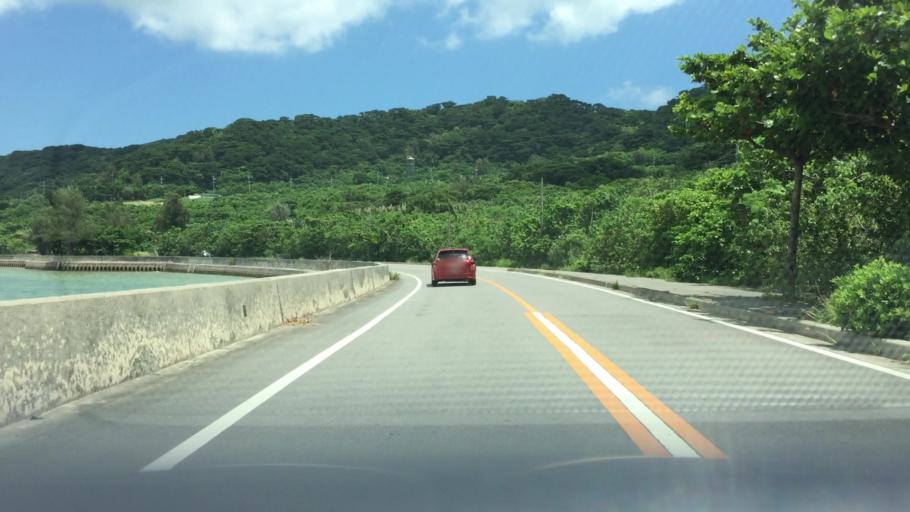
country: JP
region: Okinawa
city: Ishigaki
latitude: 24.4296
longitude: 124.1247
